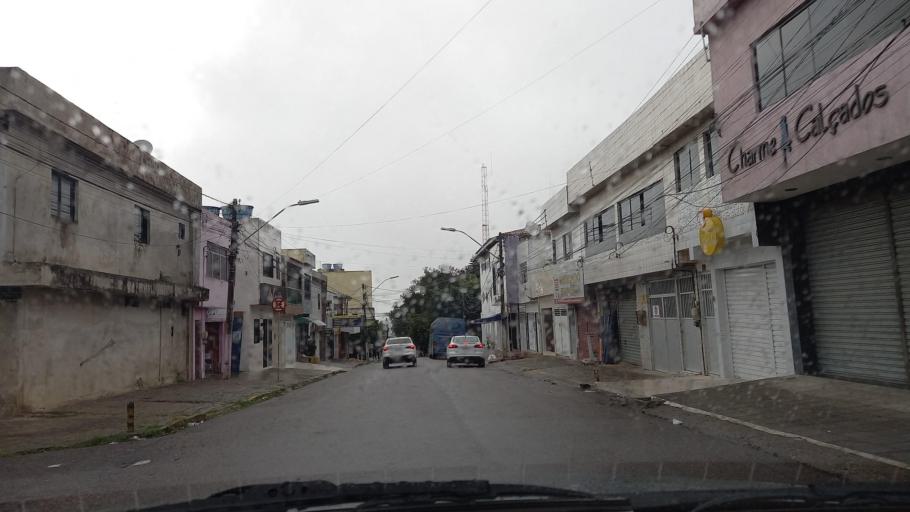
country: BR
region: Pernambuco
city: Garanhuns
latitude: -8.8827
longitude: -36.4973
